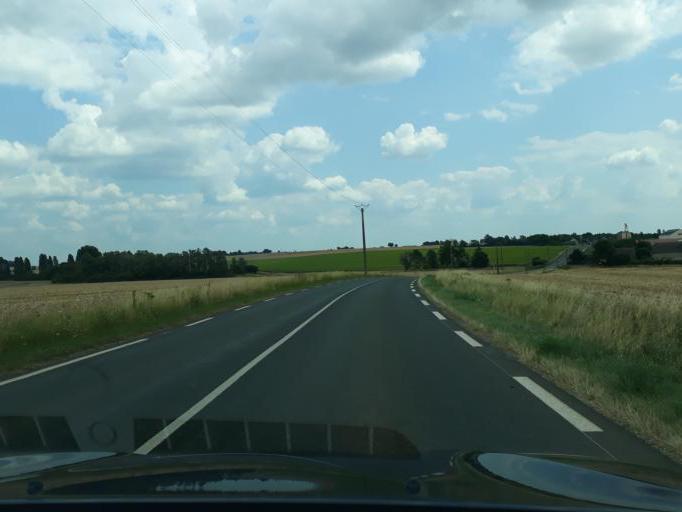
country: FR
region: Centre
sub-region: Departement du Cher
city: Baugy
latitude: 47.0099
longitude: 2.7354
